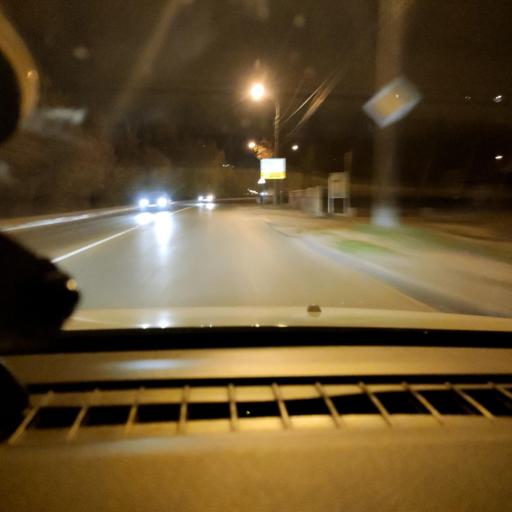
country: RU
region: Samara
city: Rozhdestveno
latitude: 53.1607
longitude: 50.0759
